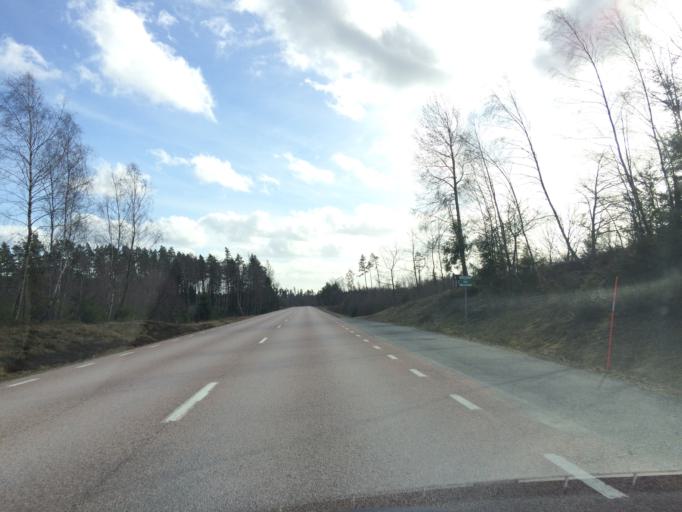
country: SE
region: Kronoberg
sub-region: Markaryds Kommun
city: Stromsnasbruk
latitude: 56.8004
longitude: 13.5613
